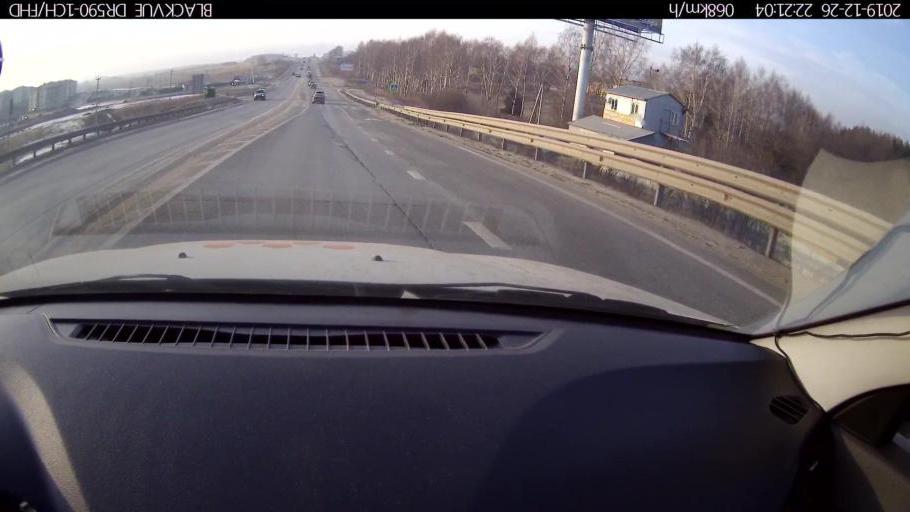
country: RU
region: Nizjnij Novgorod
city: Burevestnik
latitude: 56.2150
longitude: 43.9050
